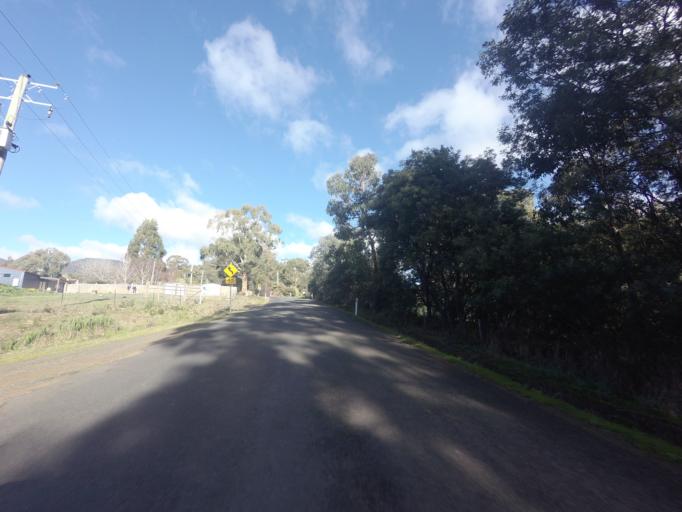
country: AU
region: Tasmania
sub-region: Derwent Valley
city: New Norfolk
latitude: -42.8041
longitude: 147.1375
